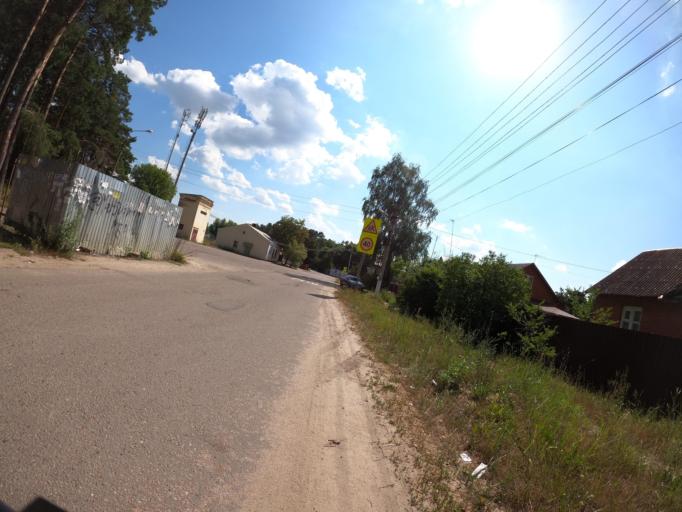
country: RU
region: Moskovskaya
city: Peski
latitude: 55.2610
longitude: 38.7672
